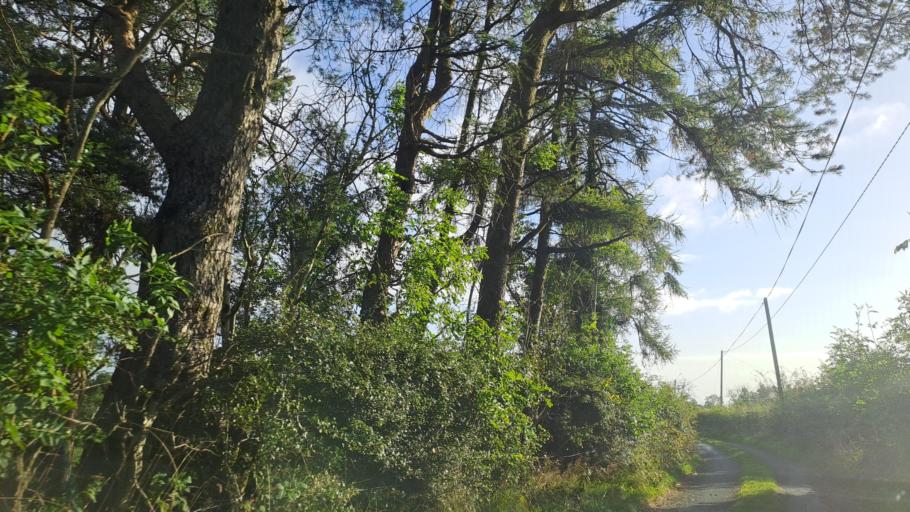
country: IE
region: Ulster
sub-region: An Cabhan
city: Kingscourt
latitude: 53.9488
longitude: -6.8642
